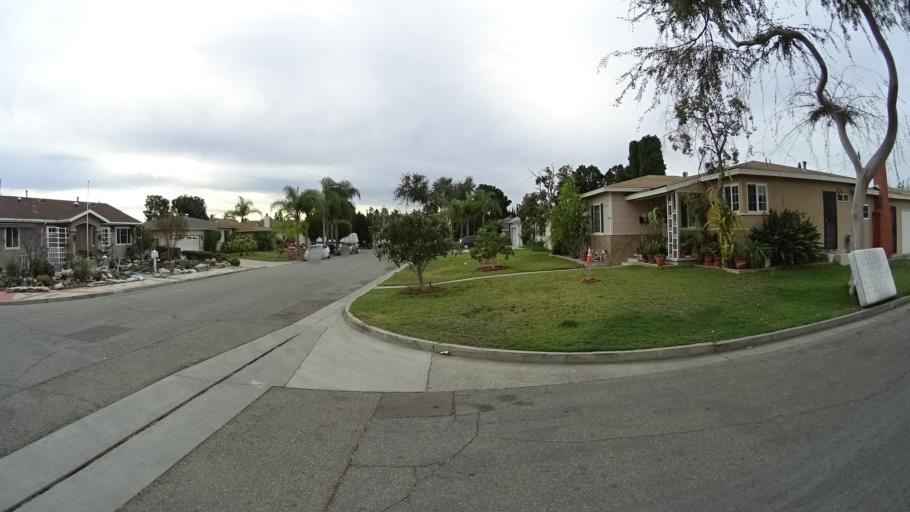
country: US
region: California
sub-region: Orange County
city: Garden Grove
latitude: 33.7803
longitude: -117.9297
